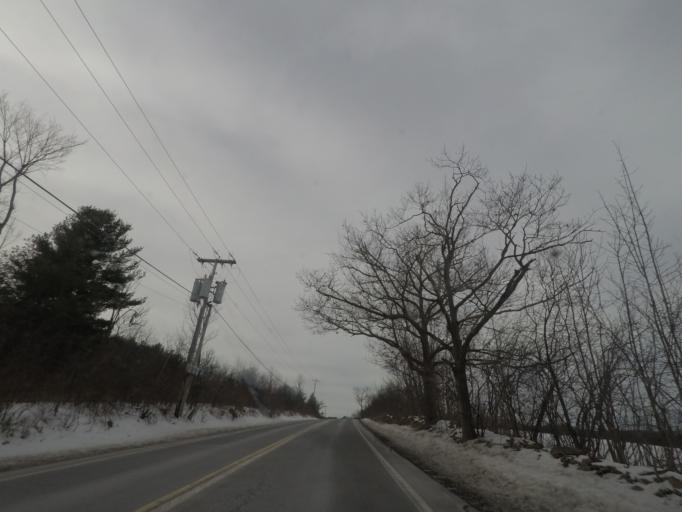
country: US
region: New York
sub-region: Albany County
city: Altamont
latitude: 42.6767
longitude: -74.0815
